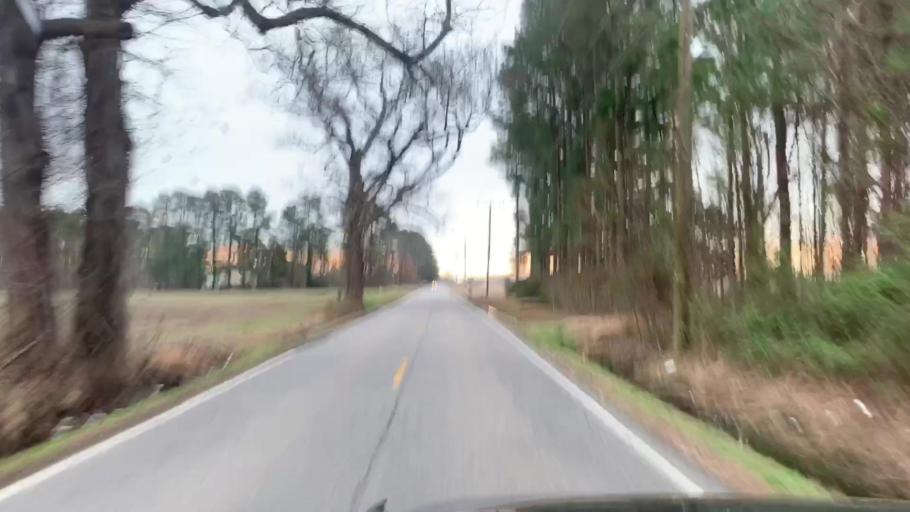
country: US
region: North Carolina
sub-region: Currituck County
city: Moyock
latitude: 36.6316
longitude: -76.1791
